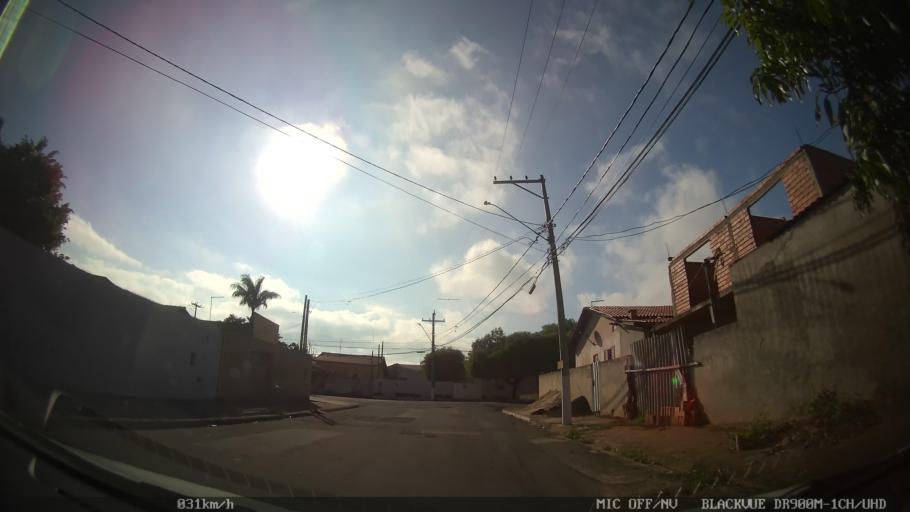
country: BR
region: Sao Paulo
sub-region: Hortolandia
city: Hortolandia
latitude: -22.9008
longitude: -47.1763
